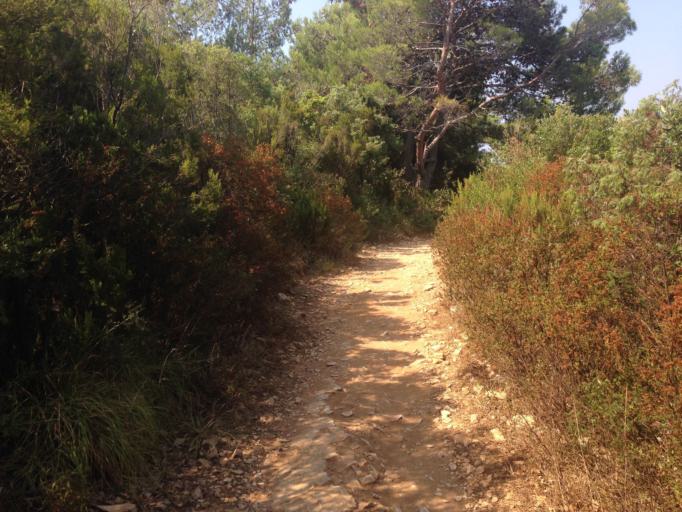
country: HR
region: Istarska
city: Medulin
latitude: 44.7849
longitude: 13.9057
